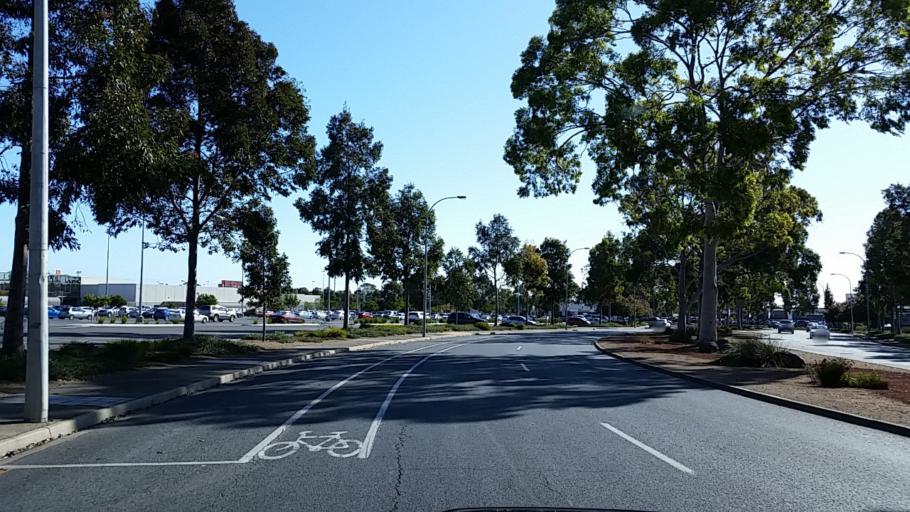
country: AU
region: South Australia
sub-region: Salisbury
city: Elizabeth
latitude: -34.7154
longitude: 138.6691
